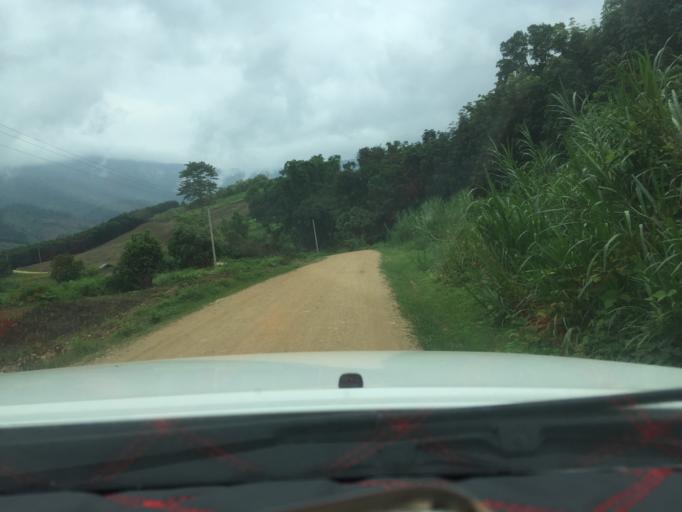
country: TH
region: Phayao
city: Phu Sang
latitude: 19.7431
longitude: 100.4553
